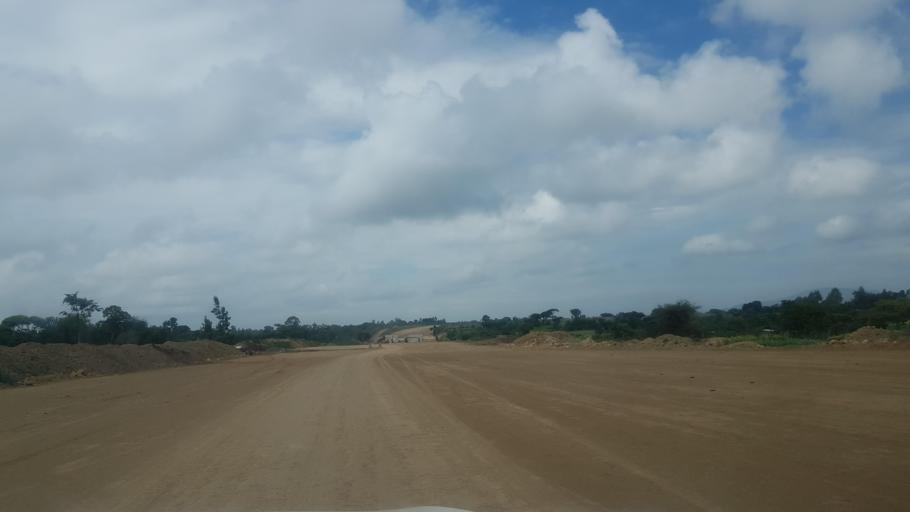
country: ET
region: Oromiya
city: Shashemene
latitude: 7.2534
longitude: 38.5927
